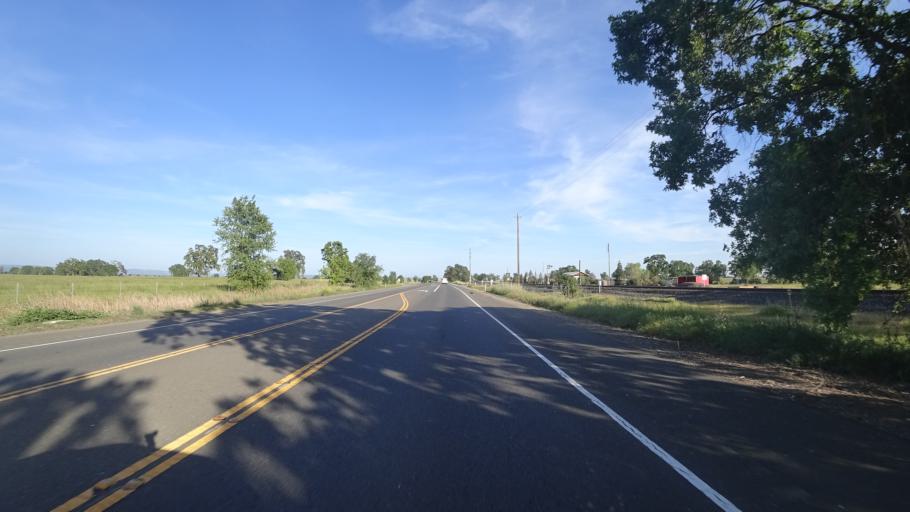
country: US
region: California
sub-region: Placer County
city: Sheridan
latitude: 38.9341
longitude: -121.3465
